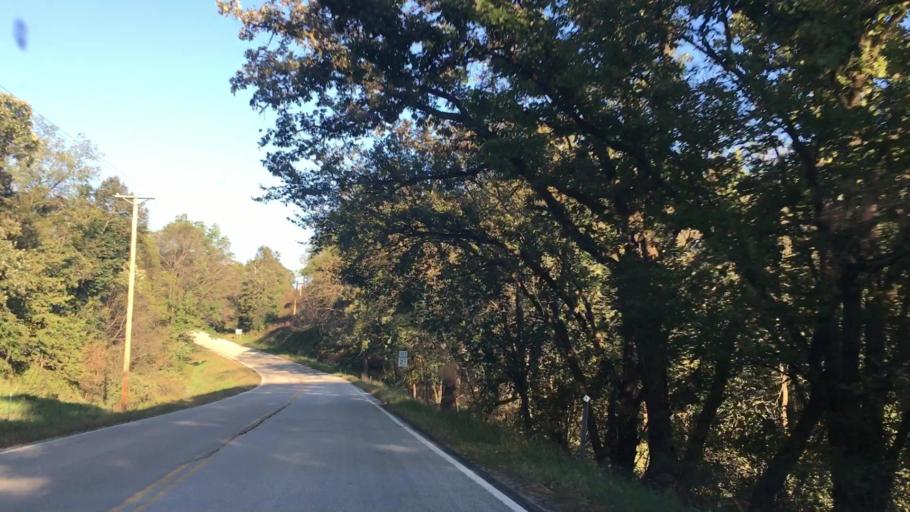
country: US
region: Minnesota
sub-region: Fillmore County
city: Chatfield
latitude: 43.8180
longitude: -92.0431
